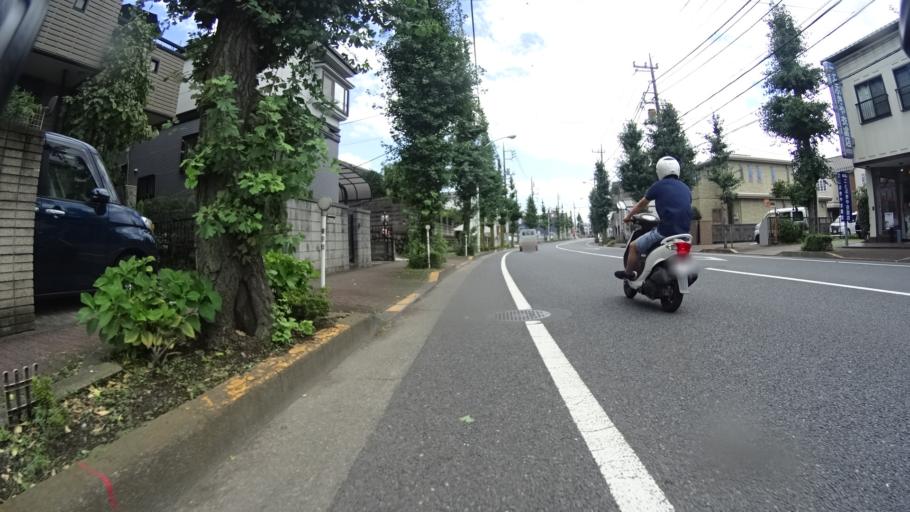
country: JP
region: Tokyo
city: Fussa
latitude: 35.7462
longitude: 139.3231
